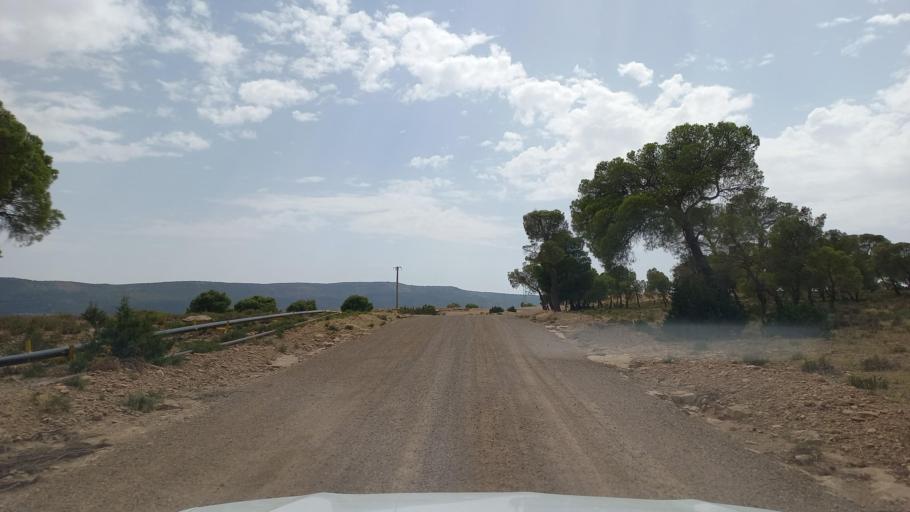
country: TN
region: Al Qasrayn
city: Kasserine
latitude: 35.3791
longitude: 8.8797
